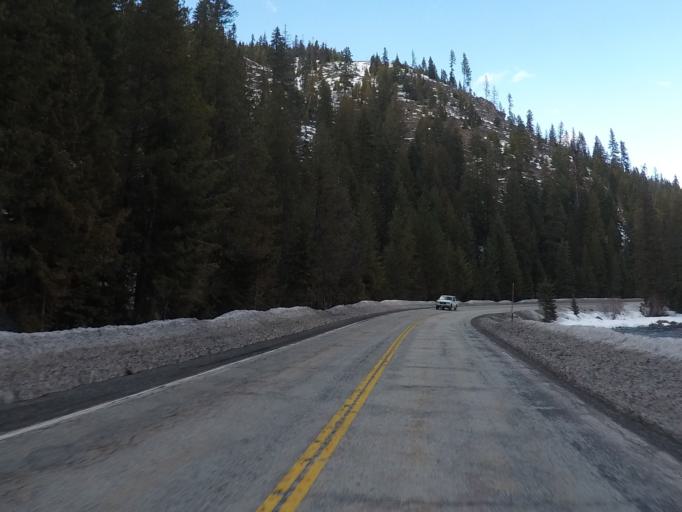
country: US
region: Montana
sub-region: Ravalli County
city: Stevensville
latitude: 46.5570
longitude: -114.6631
